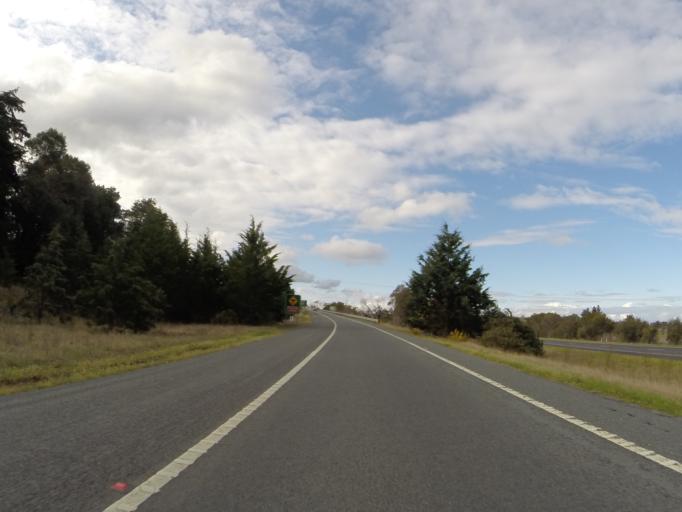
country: AU
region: New South Wales
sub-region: Wingecarribee
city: Bundanoon
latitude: -34.5888
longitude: 150.2480
